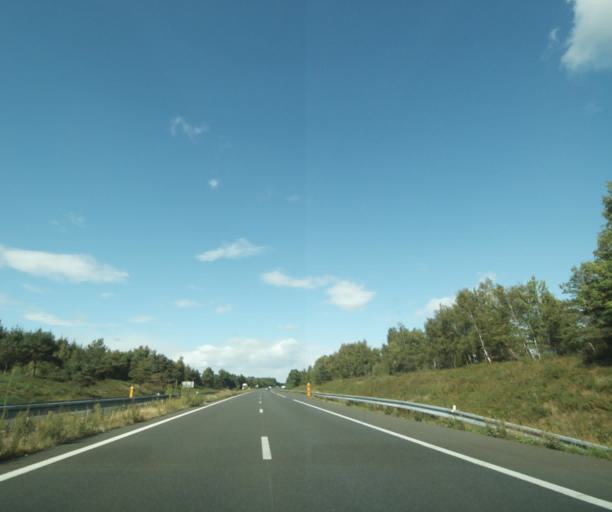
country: FR
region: Centre
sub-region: Departement du Loiret
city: Saint-Hilaire-Saint-Mesmin
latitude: 47.8279
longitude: 1.8602
